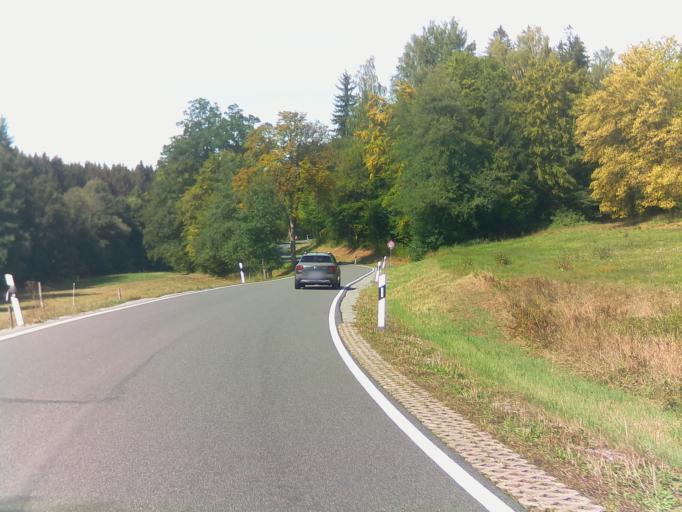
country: DE
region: Thuringia
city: Schwarza
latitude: 50.6439
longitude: 10.5218
